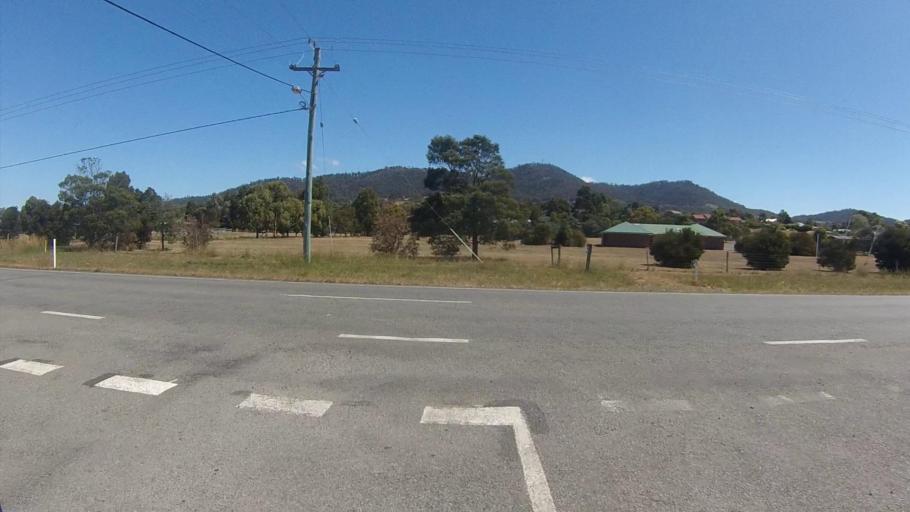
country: AU
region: Tasmania
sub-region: Clarence
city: Seven Mile Beach
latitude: -42.8490
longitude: 147.4838
